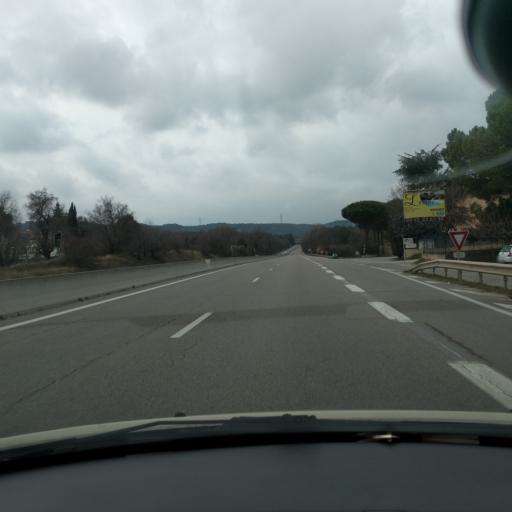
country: FR
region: Provence-Alpes-Cote d'Azur
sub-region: Departement des Bouches-du-Rhone
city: Simiane-Collongue
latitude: 43.4414
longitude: 5.4343
